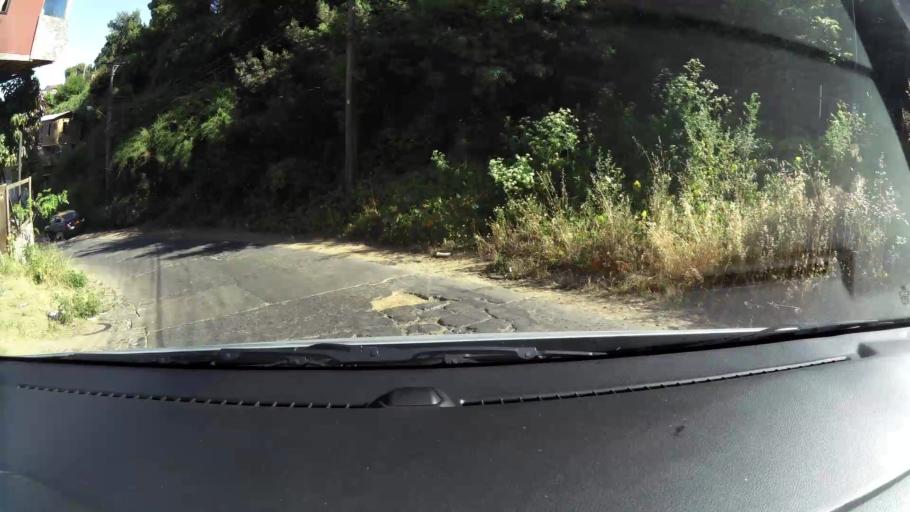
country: CL
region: Valparaiso
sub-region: Provincia de Valparaiso
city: Valparaiso
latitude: -33.0622
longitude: -71.5881
